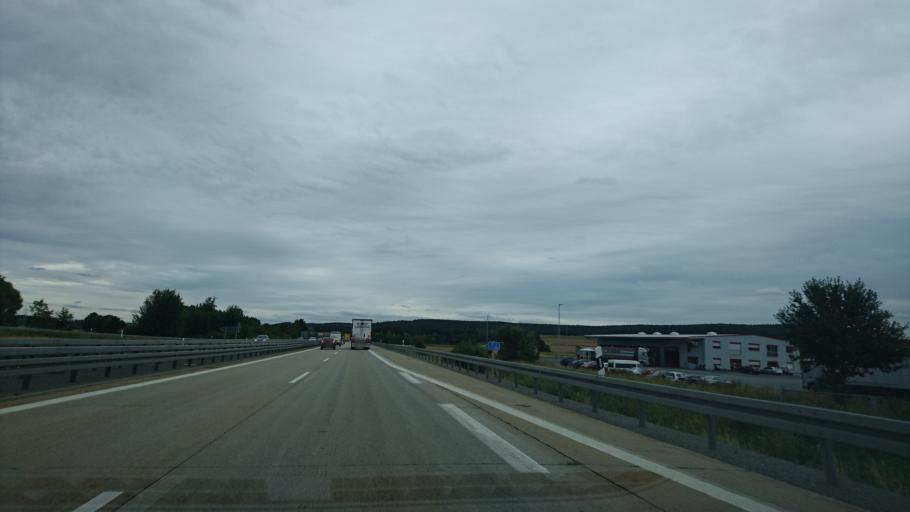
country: DE
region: Bavaria
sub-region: Upper Palatinate
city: Luhe-Wildenau
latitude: 49.5939
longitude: 12.1424
